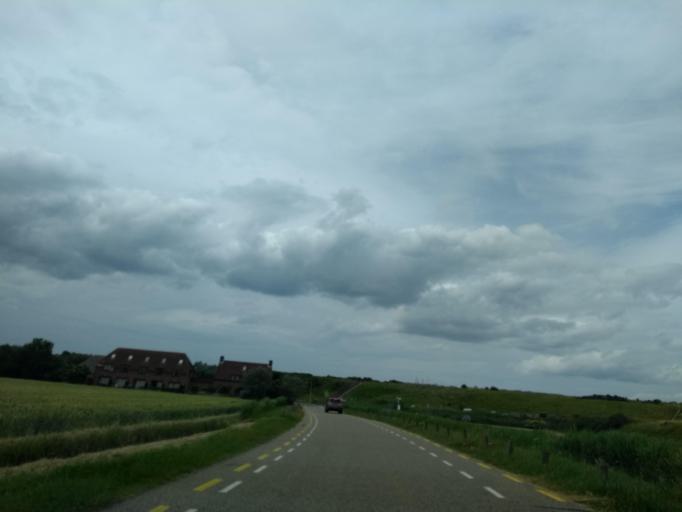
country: NL
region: Zeeland
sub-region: Gemeente Sluis
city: Sluis
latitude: 51.3878
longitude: 3.4264
